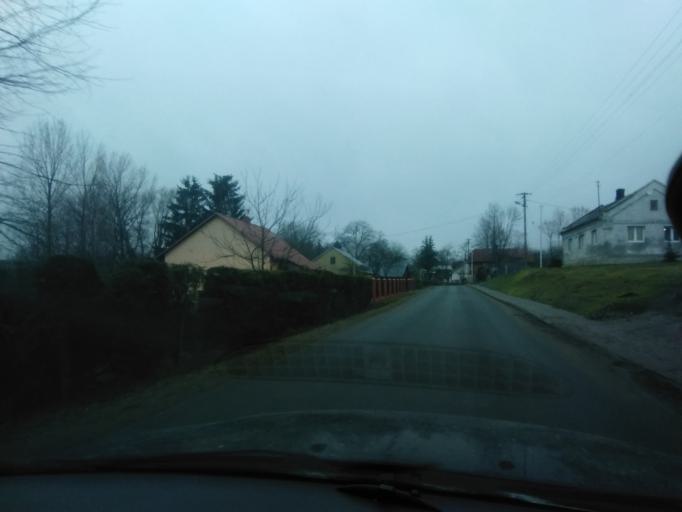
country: PL
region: Subcarpathian Voivodeship
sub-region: Powiat jaroslawski
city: Rokietnica
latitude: 49.9169
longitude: 22.6157
